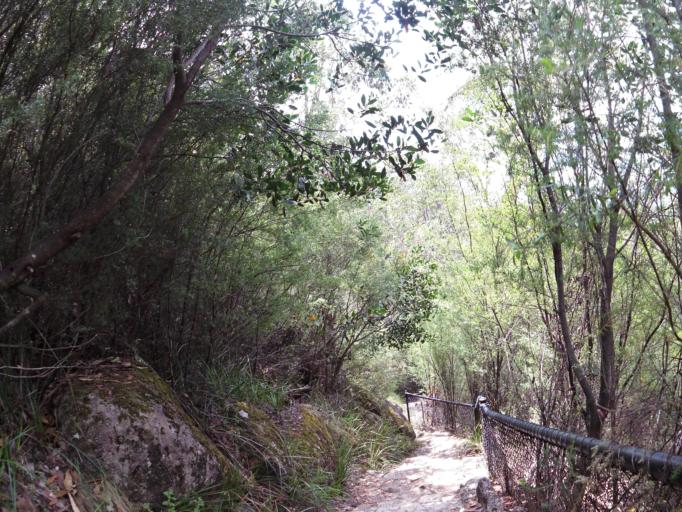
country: AU
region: Victoria
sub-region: Alpine
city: Mount Beauty
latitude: -36.7182
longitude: 146.8380
